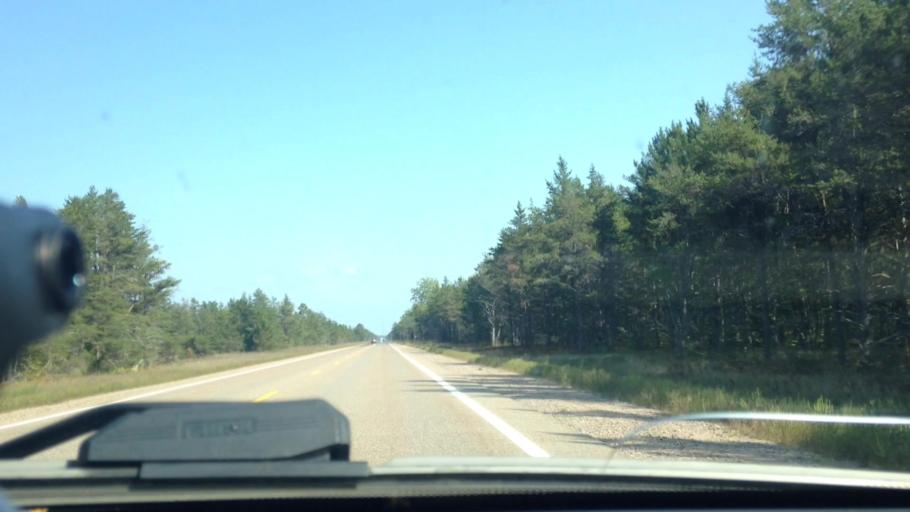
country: US
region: Michigan
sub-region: Mackinac County
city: Saint Ignace
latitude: 46.3585
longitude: -84.8537
